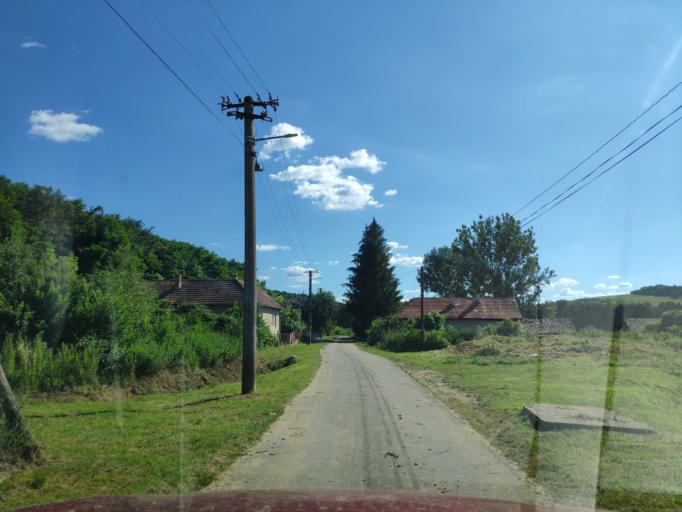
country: SK
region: Banskobystricky
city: Rimavska Sobota
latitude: 48.2624
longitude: 20.1151
